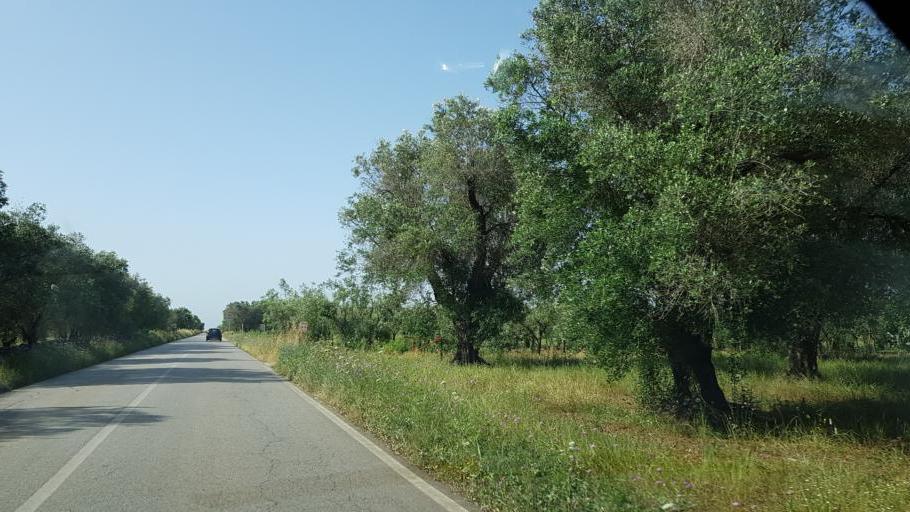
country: IT
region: Apulia
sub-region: Provincia di Brindisi
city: Mesagne
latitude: 40.5152
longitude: 17.8261
